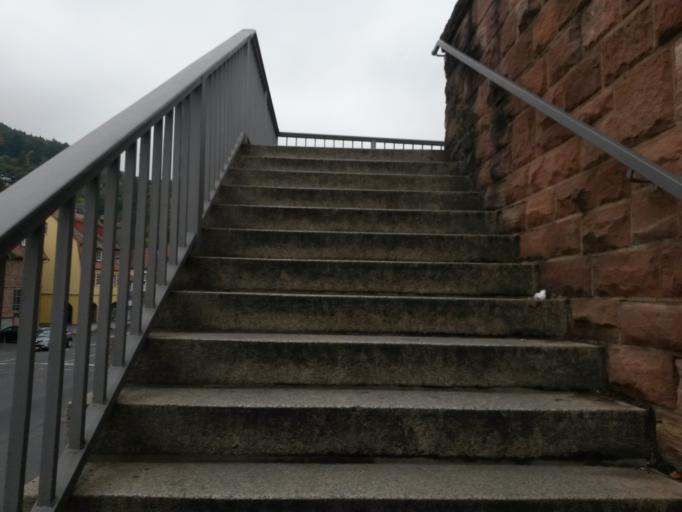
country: DE
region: Bavaria
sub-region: Regierungsbezirk Unterfranken
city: Miltenberg
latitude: 49.7016
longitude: 9.2560
